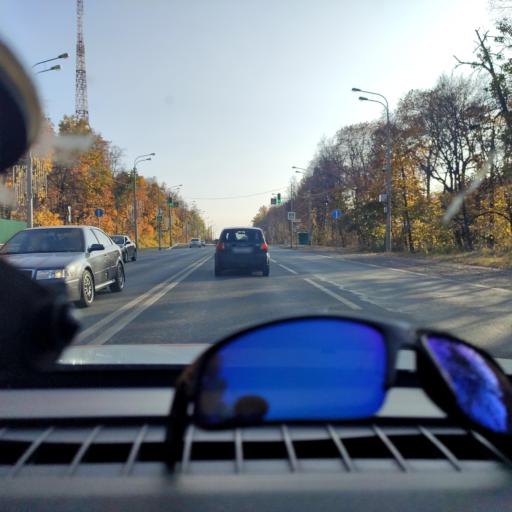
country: RU
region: Samara
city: Samara
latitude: 53.2960
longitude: 50.2254
